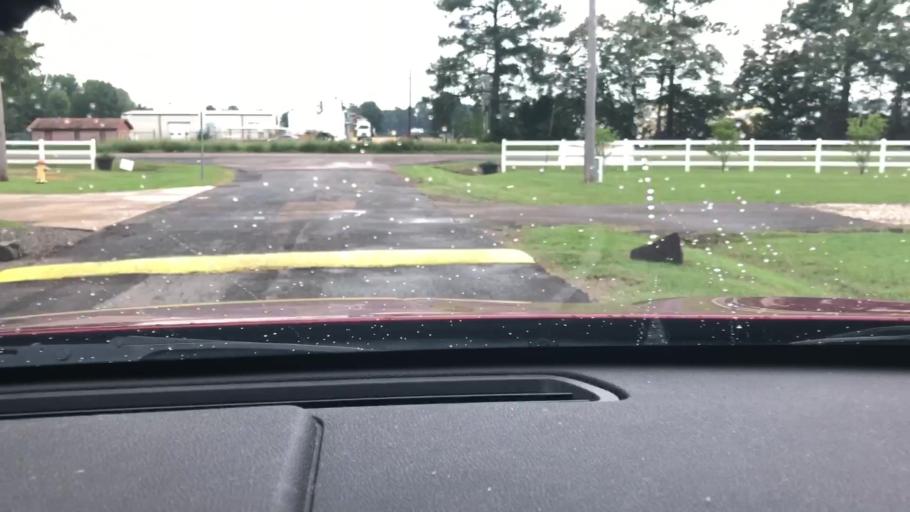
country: US
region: Texas
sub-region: Bowie County
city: Nash
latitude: 33.4425
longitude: -94.1382
